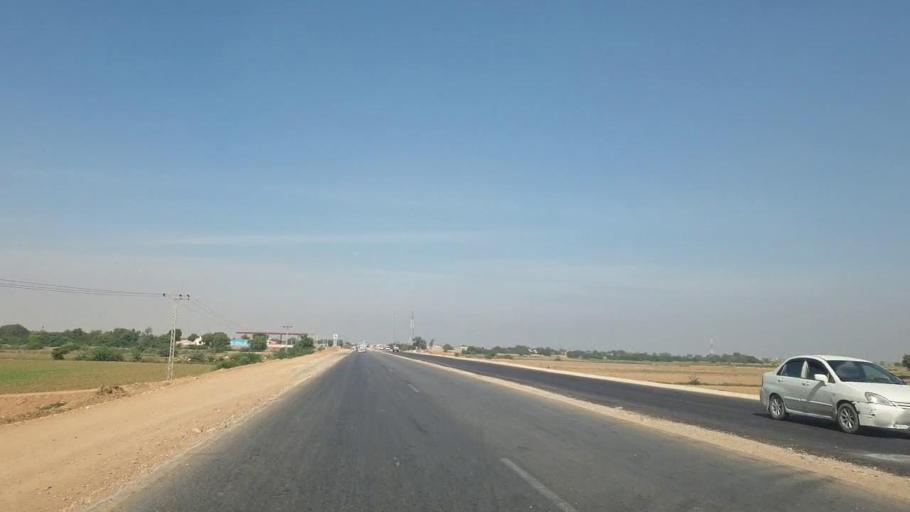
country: PK
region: Sindh
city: Matiari
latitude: 25.6421
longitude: 68.3013
